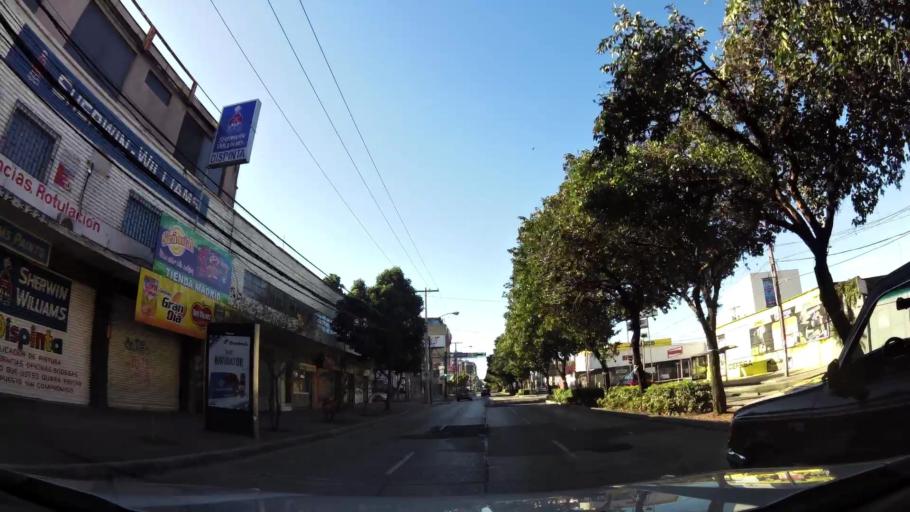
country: GT
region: Guatemala
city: Guatemala City
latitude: 14.6125
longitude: -90.5184
